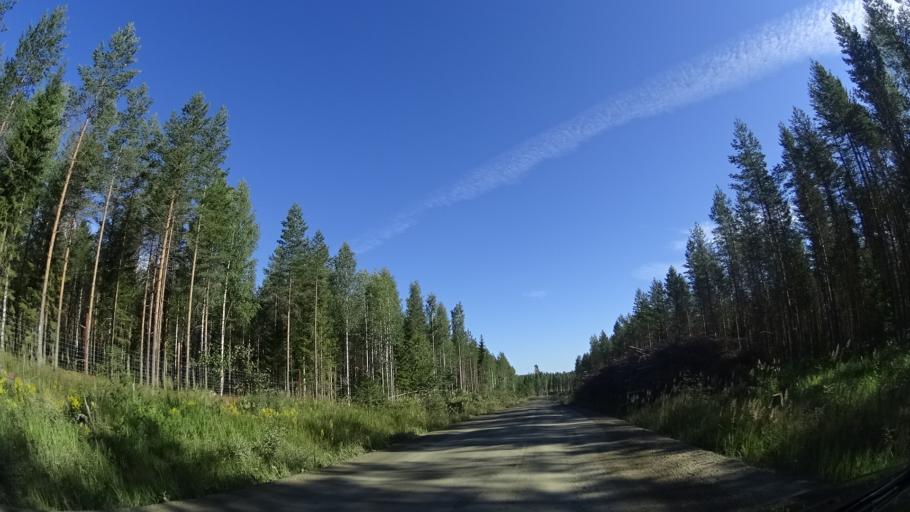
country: FI
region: Central Finland
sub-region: Jyvaeskylae
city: Petaejaevesi
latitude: 62.3103
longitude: 25.3435
